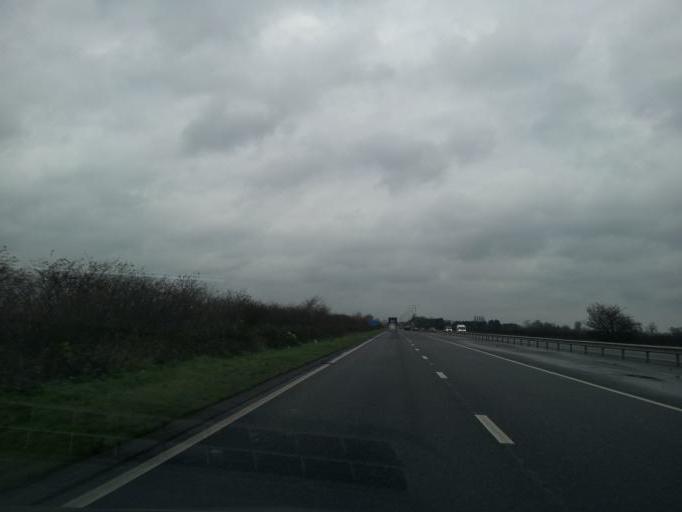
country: GB
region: England
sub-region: Leicestershire
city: Queniborough
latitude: 52.7368
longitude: -1.0679
